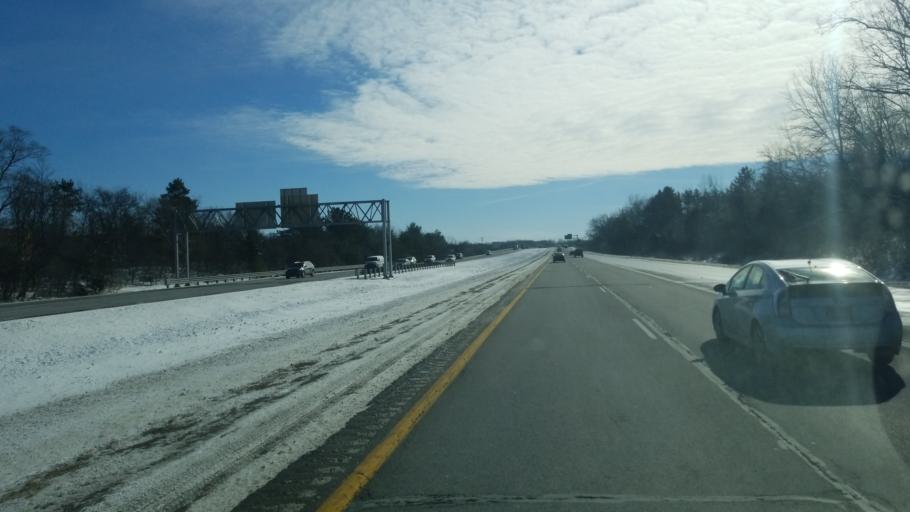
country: US
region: Michigan
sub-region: Washtenaw County
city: Ann Arbor
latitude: 42.2513
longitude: -83.6839
